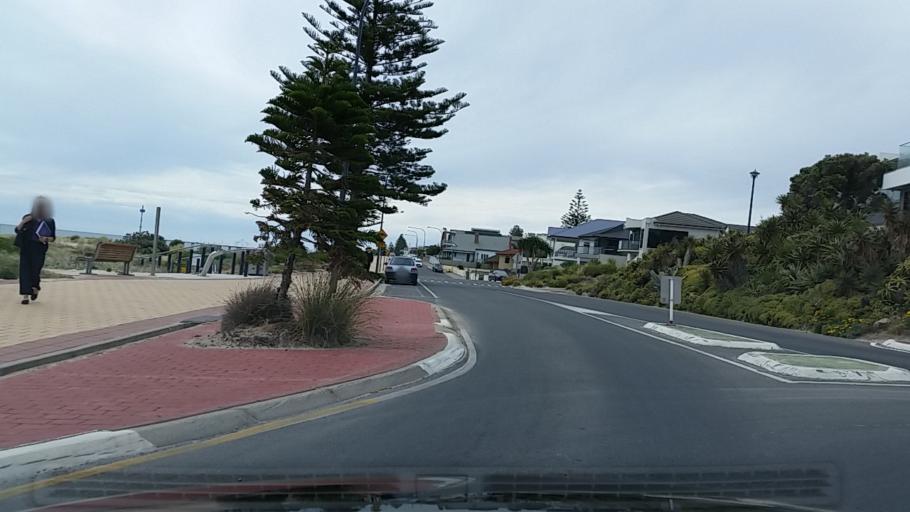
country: AU
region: South Australia
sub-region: Adelaide
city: Brighton
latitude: -35.0230
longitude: 138.5165
